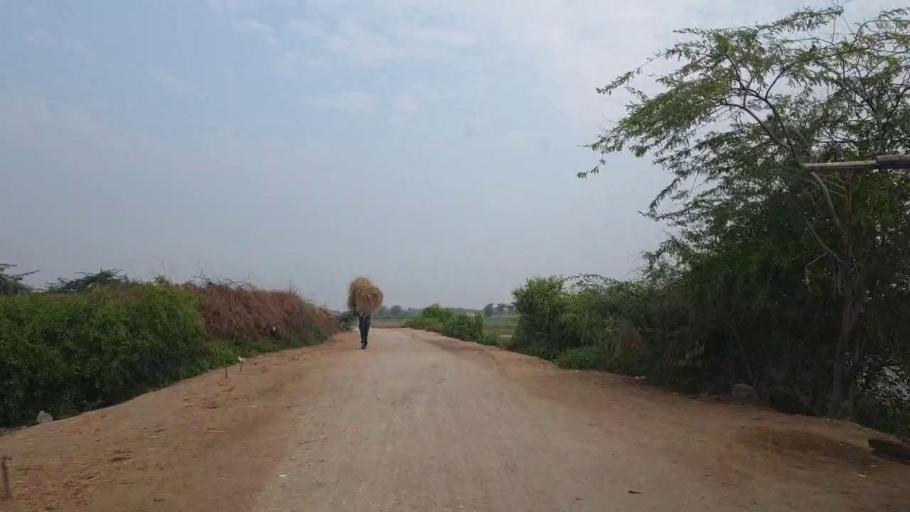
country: PK
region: Sindh
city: Tando Bago
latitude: 24.7957
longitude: 68.8761
